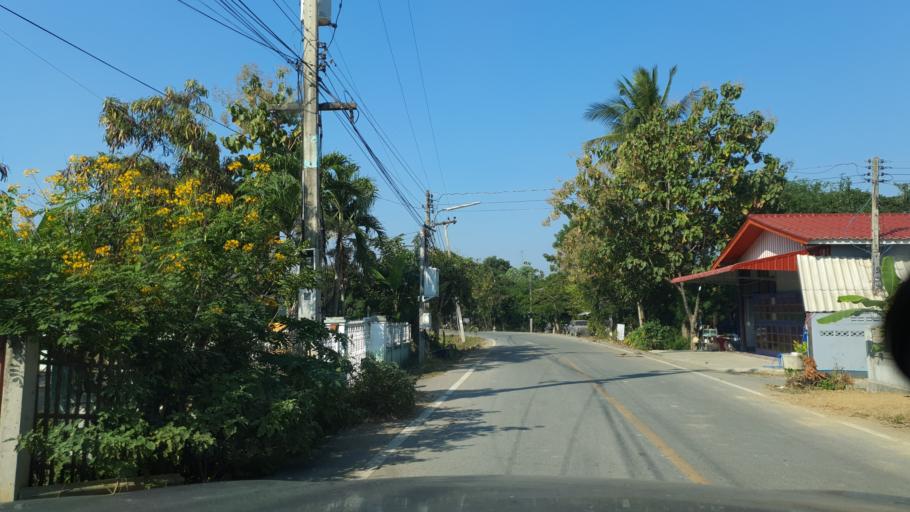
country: TH
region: Lamphun
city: Ban Thi
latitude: 18.6823
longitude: 99.1223
